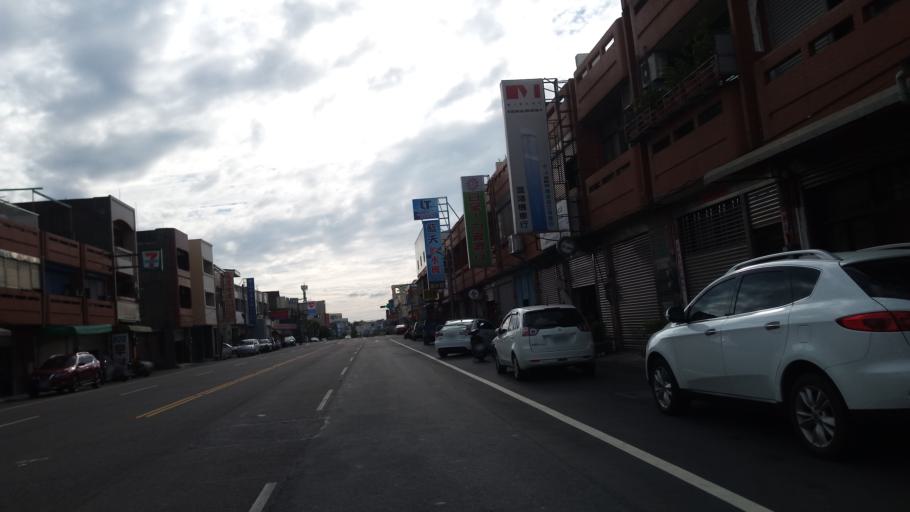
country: TW
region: Taiwan
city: Fengyuan
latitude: 24.3915
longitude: 120.6545
